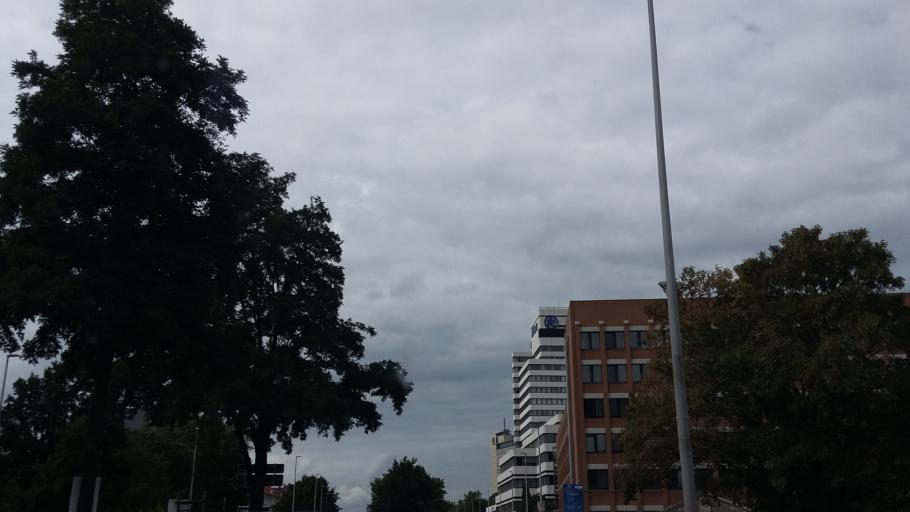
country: DE
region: Lower Saxony
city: Hannover
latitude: 52.3745
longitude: 9.7281
